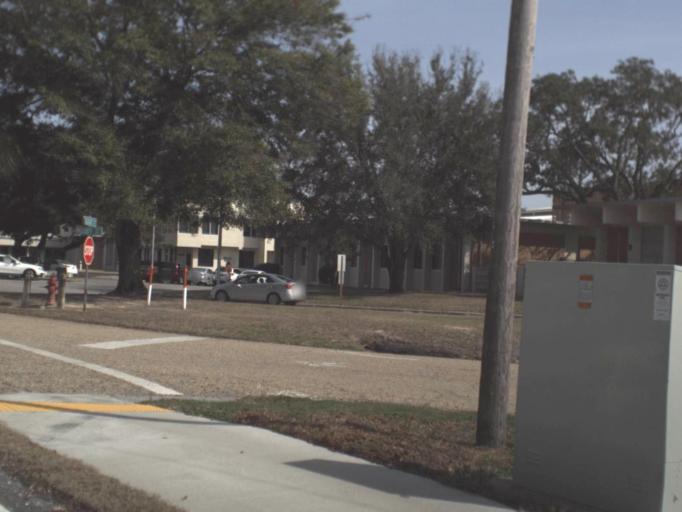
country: US
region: Florida
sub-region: Bay County
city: Upper Grand Lagoon
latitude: 30.1867
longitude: -85.7301
